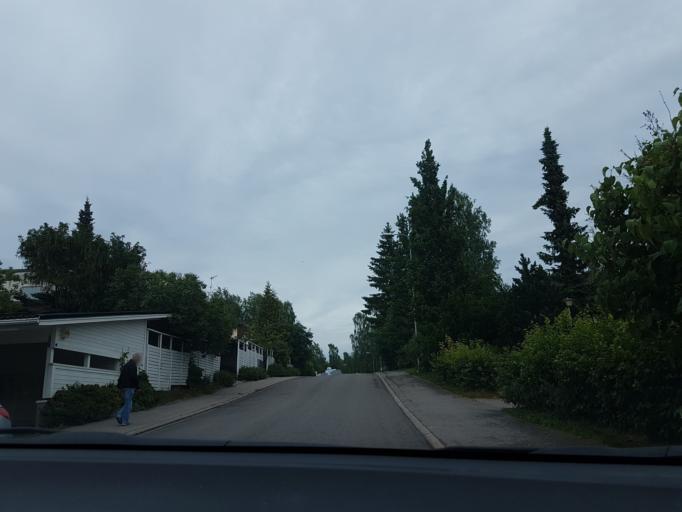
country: FI
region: Uusimaa
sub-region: Helsinki
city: Vantaa
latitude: 60.2104
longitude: 25.1245
